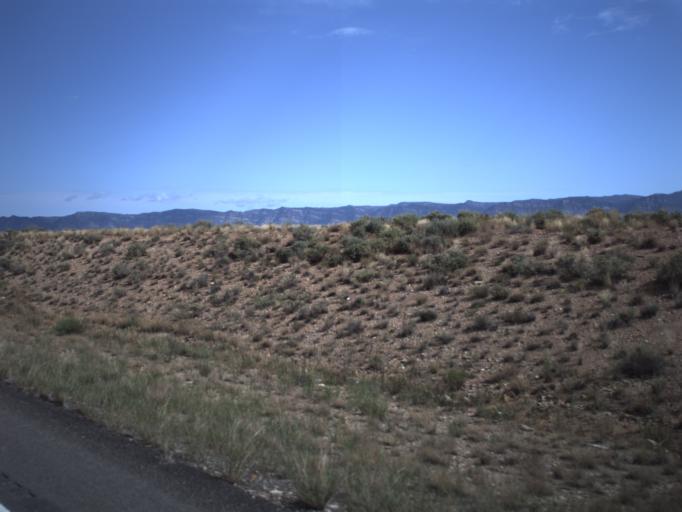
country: US
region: Utah
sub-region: Carbon County
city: East Carbon City
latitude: 39.5038
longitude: -110.5303
